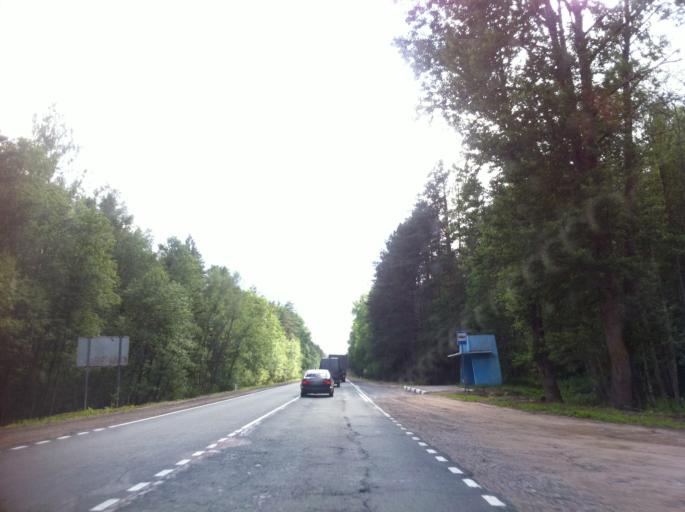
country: RU
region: Pskov
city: Strugi-Krasnyye
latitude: 57.9789
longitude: 28.7736
